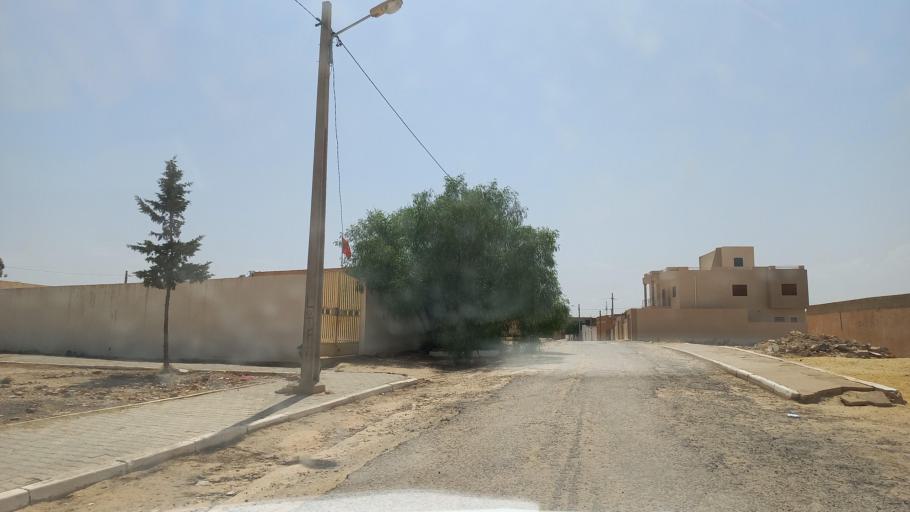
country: TN
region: Al Qasrayn
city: Kasserine
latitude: 35.2514
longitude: 9.0274
